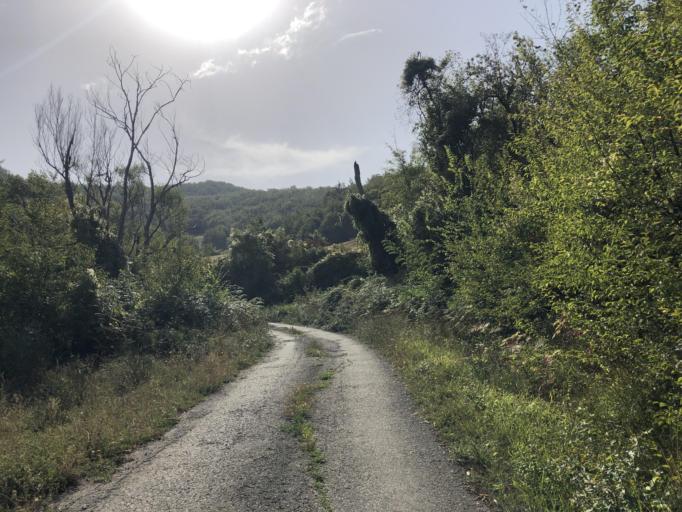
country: IT
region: Emilia-Romagna
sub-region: Forli-Cesena
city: Portico e San Benedetto
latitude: 44.0175
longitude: 11.7857
